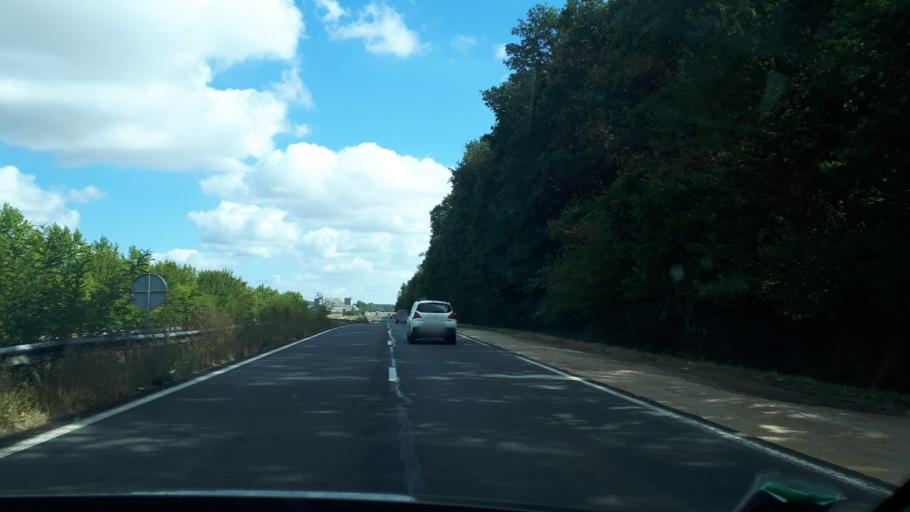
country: FR
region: Centre
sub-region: Departement du Loir-et-Cher
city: Saint-Ouen
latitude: 47.8365
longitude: 1.0869
